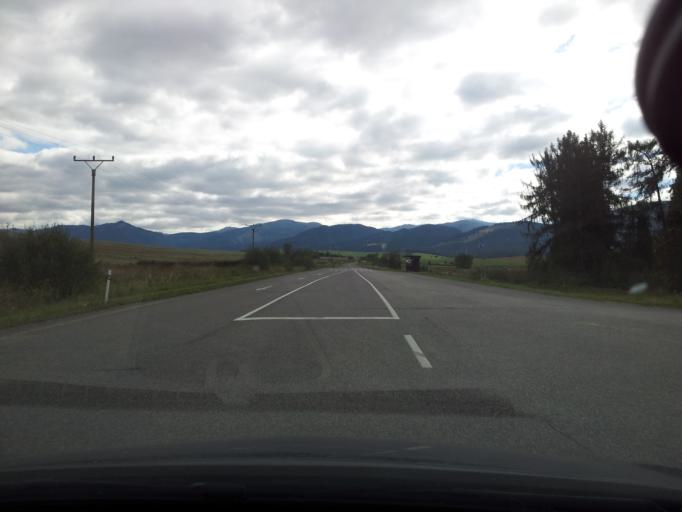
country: SK
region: Zilinsky
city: Ruzomberok
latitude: 49.0700
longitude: 19.4387
